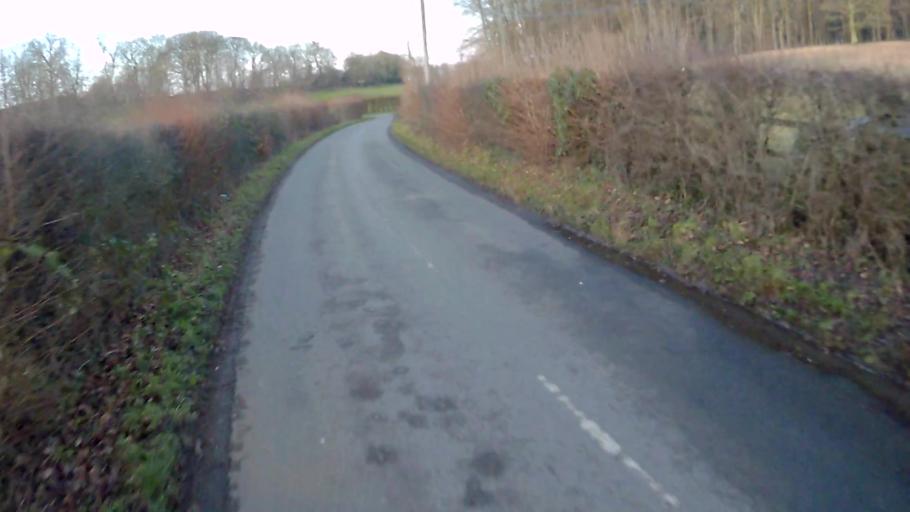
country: GB
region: England
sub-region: Hampshire
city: Overton
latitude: 51.2372
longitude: -1.2209
